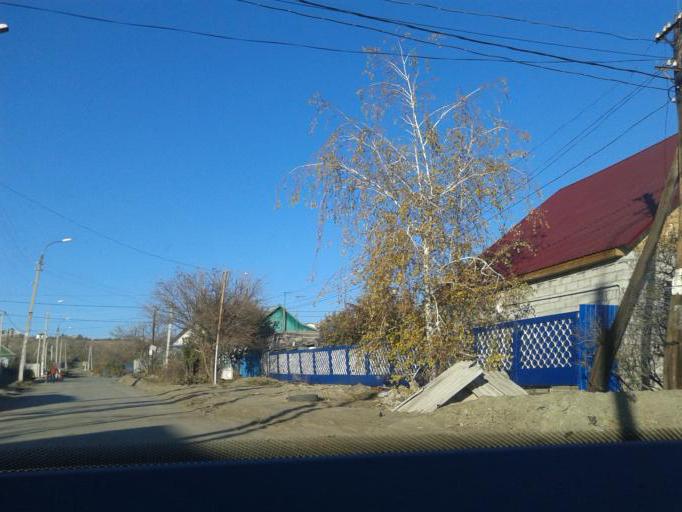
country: RU
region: Volgograd
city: Volgograd
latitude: 48.6110
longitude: 44.4147
